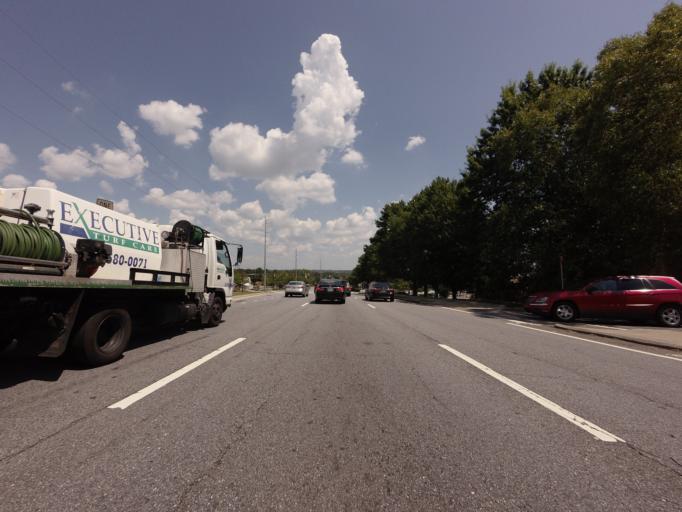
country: US
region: Georgia
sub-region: Fulton County
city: Johns Creek
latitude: 34.0170
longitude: -84.1888
